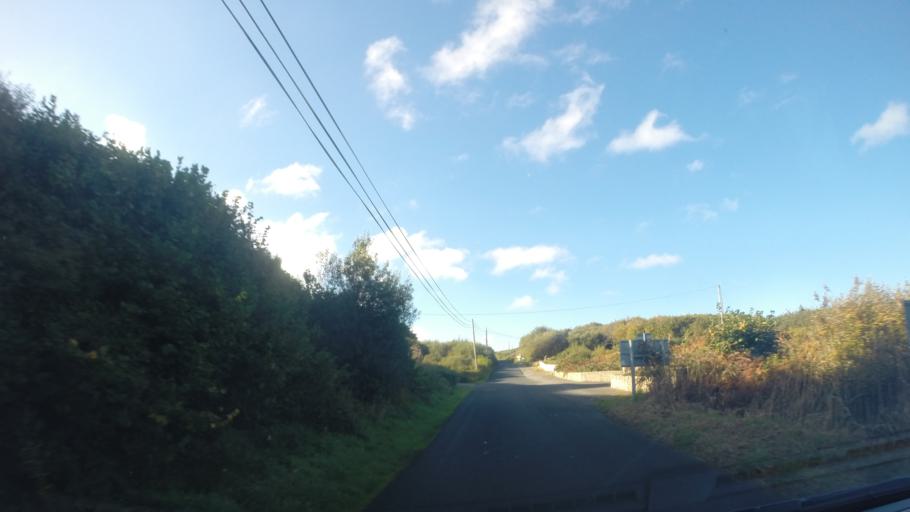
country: IE
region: Ulster
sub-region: County Donegal
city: Dungloe
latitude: 54.8350
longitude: -8.4323
